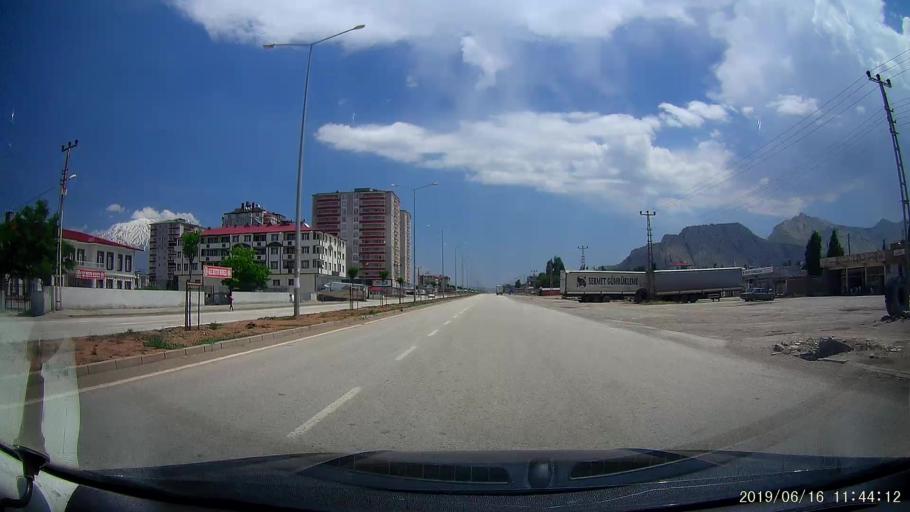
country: TR
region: Agri
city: Dogubayazit
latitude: 39.5572
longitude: 44.0860
